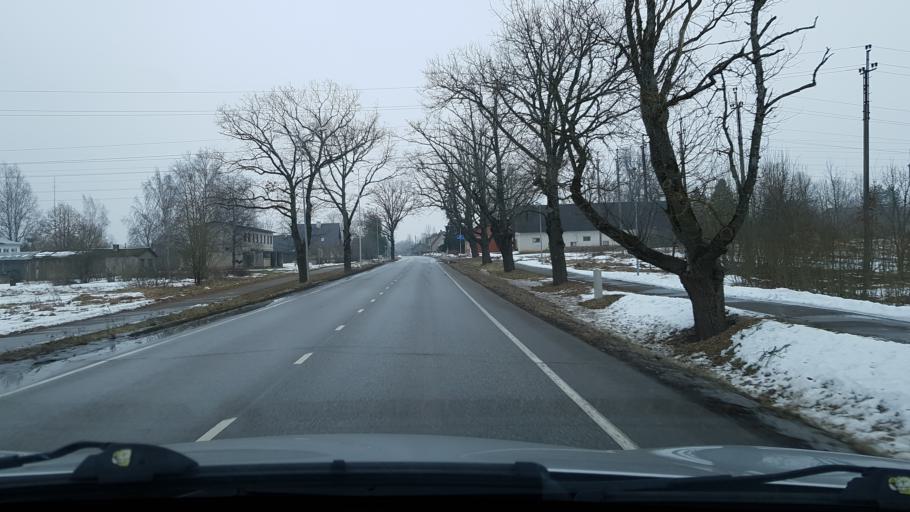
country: EE
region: Viljandimaa
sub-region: Viiratsi vald
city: Viiratsi
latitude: 58.2415
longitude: 25.8569
